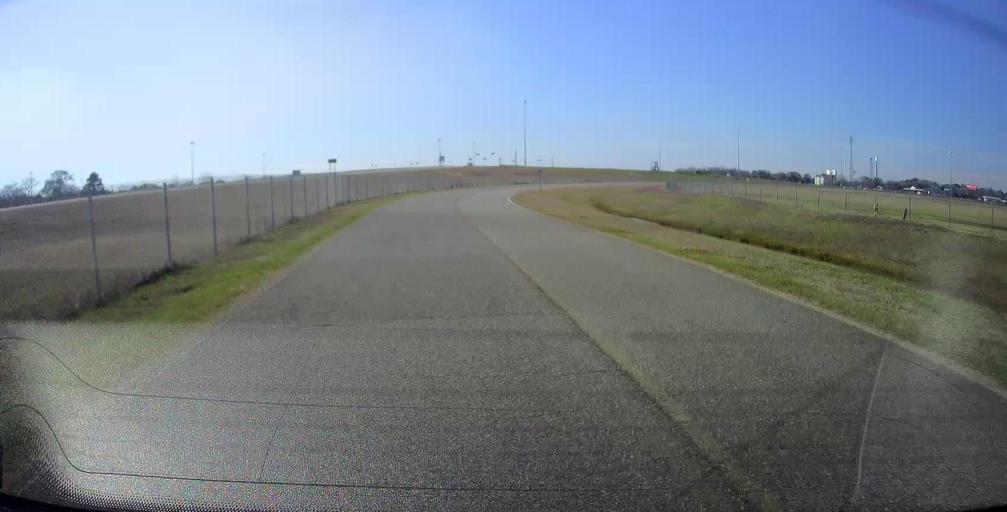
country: US
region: Georgia
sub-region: Houston County
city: Perry
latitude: 32.4318
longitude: -83.7523
